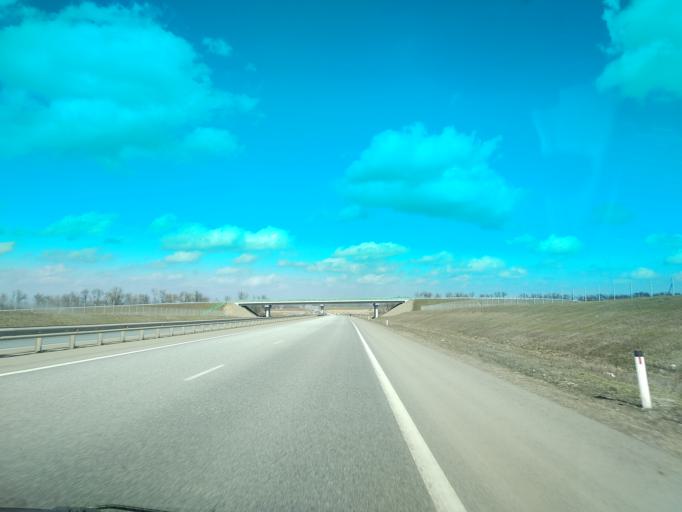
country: RU
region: Krasnodarskiy
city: Berezanskaya
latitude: 45.6642
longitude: 39.5914
